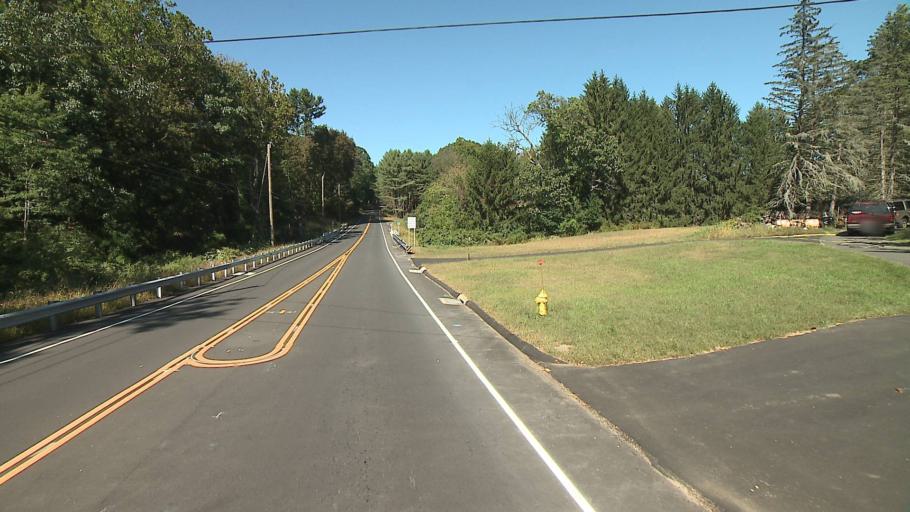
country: US
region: Connecticut
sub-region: New Haven County
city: Orange
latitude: 41.3011
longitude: -73.0181
